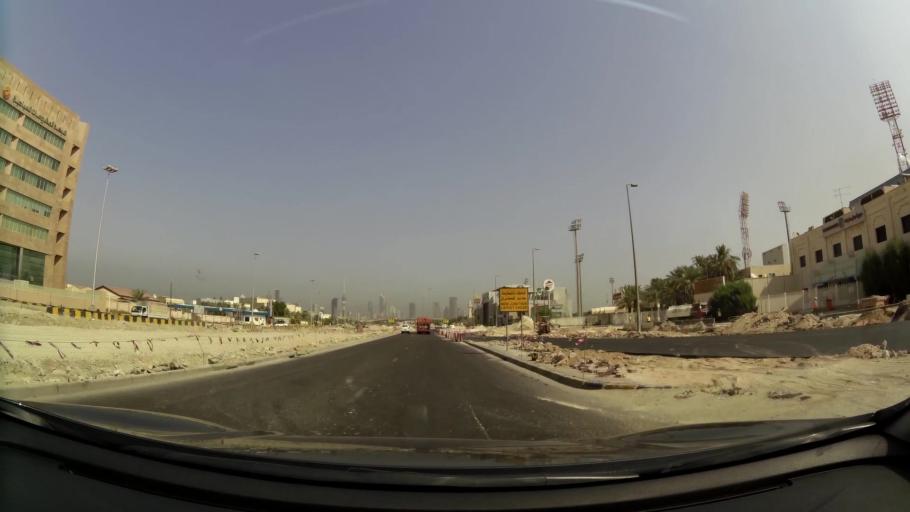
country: KW
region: Al Asimah
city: Ash Shamiyah
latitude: 29.3439
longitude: 47.9504
